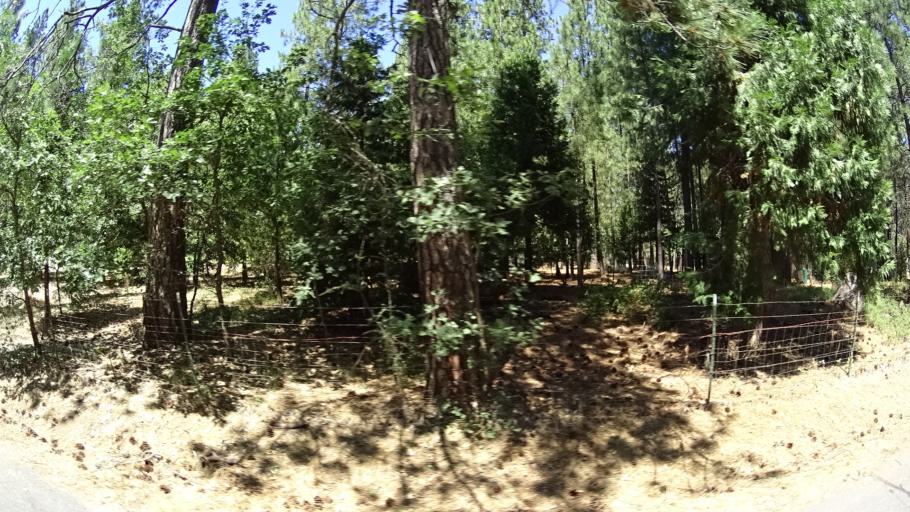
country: US
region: California
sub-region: Calaveras County
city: Mountain Ranch
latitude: 38.3301
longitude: -120.5160
